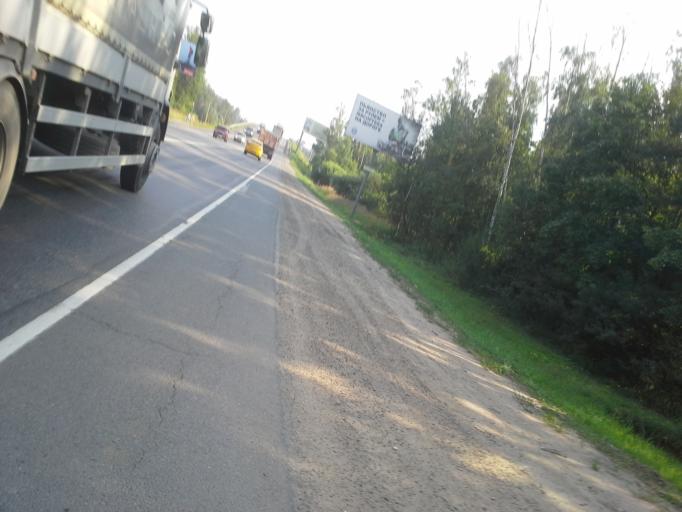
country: RU
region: Moskovskaya
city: Istra
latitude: 55.9017
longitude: 36.9448
